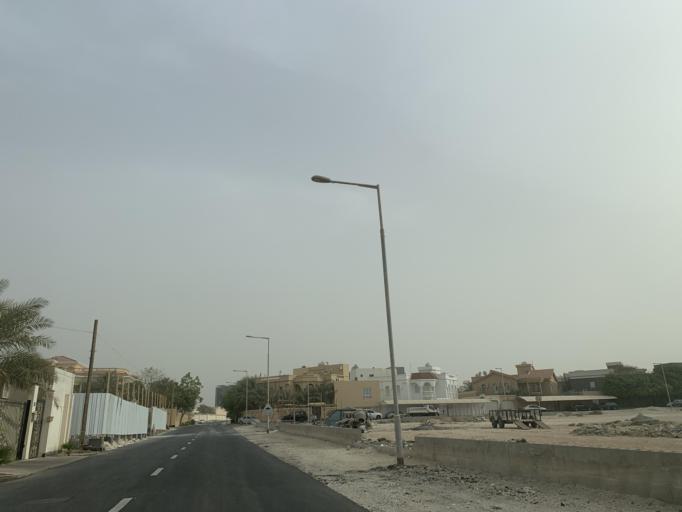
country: BH
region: Northern
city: Ar Rifa'
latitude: 26.1403
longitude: 50.5274
